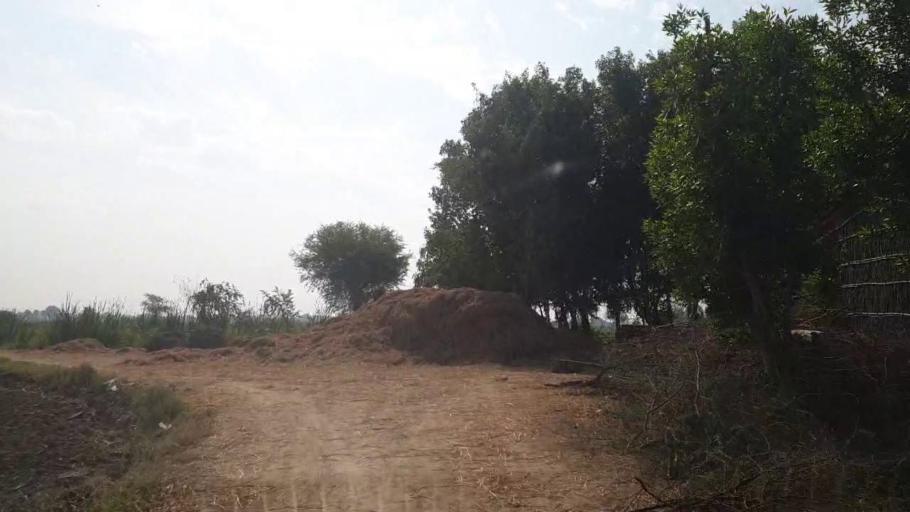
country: PK
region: Sindh
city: Tando Bago
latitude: 24.8825
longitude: 69.0035
